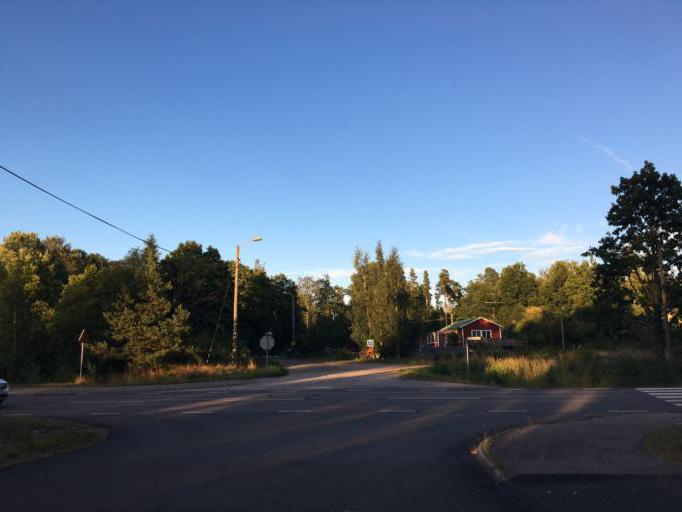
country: SE
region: Soedermanland
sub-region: Eskilstuna Kommun
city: Torshalla
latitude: 59.4354
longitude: 16.4599
